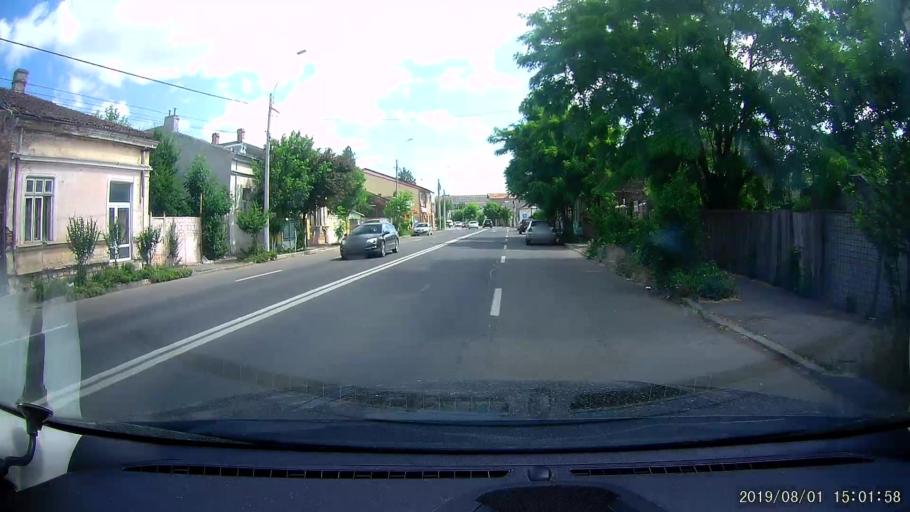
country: RO
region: Braila
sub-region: Municipiul Braila
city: Braila
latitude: 45.2696
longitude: 27.9604
